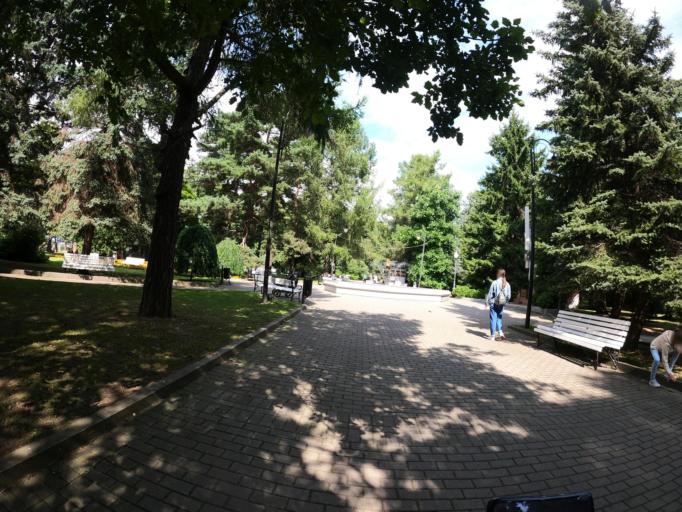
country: RU
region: Kaliningrad
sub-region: Gorod Kaliningrad
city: Kaliningrad
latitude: 54.7182
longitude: 20.4768
